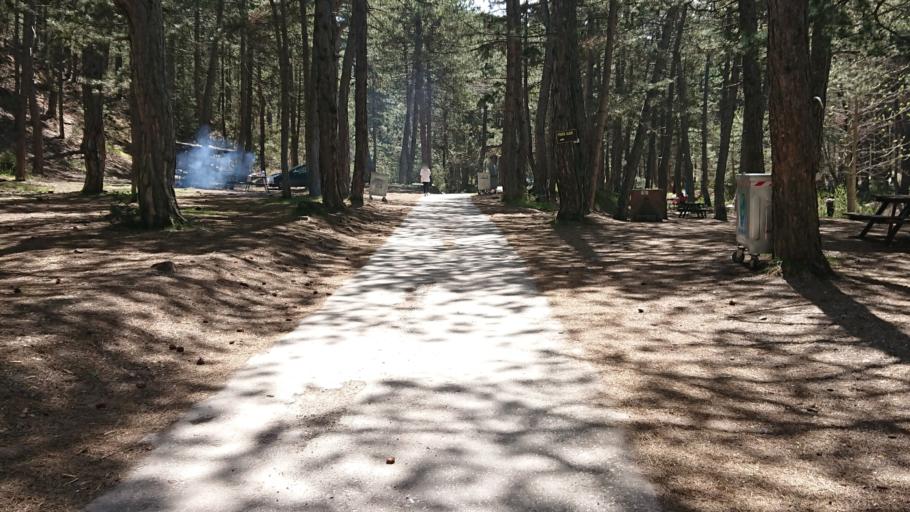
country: TR
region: Kuetahya
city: Sabuncu
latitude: 39.5125
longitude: 30.4237
